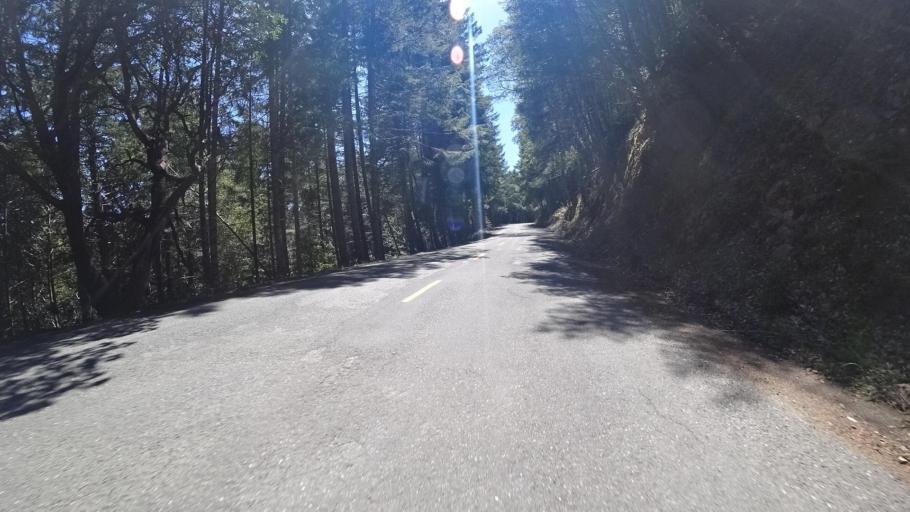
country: US
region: California
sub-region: Humboldt County
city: Rio Dell
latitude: 40.3166
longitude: -124.0593
